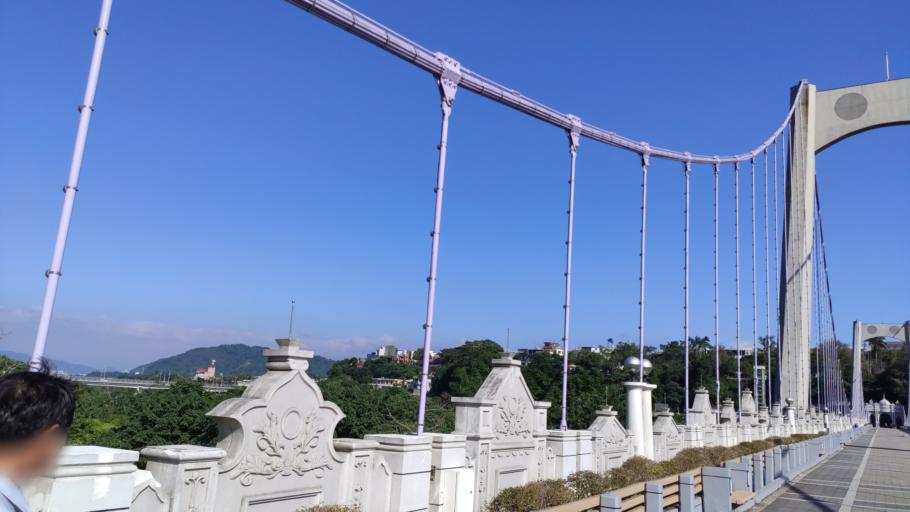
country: TW
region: Taiwan
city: Daxi
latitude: 24.8854
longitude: 121.2816
